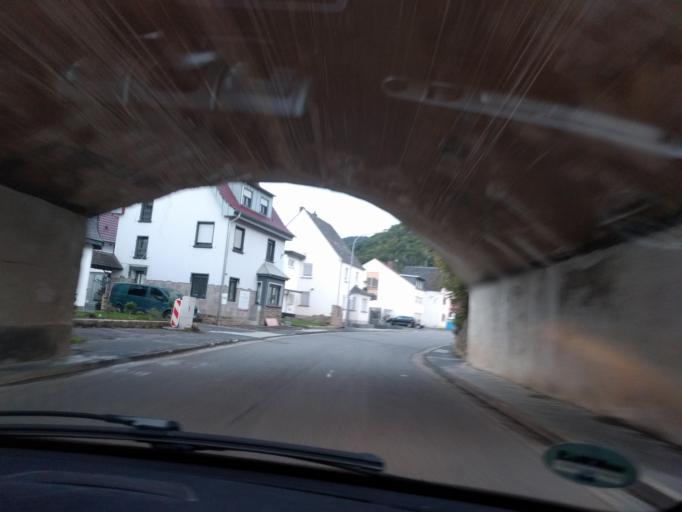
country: DE
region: Rheinland-Pfalz
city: Rech
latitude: 50.5164
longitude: 7.0380
